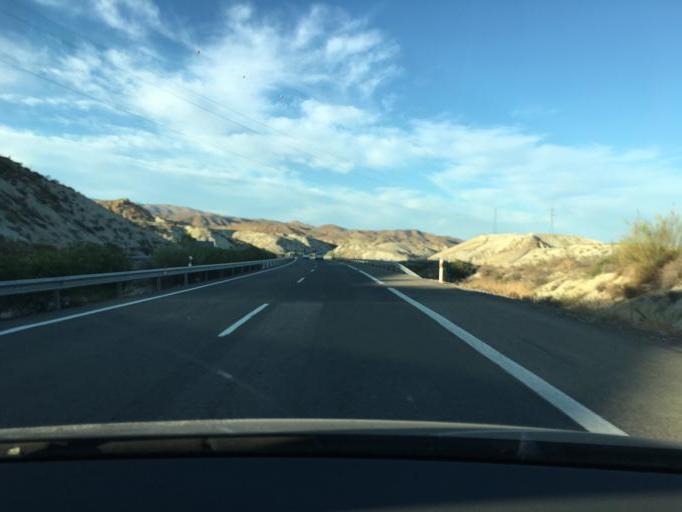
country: ES
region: Andalusia
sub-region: Provincia de Almeria
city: Bedar
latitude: 37.1143
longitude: -2.0225
